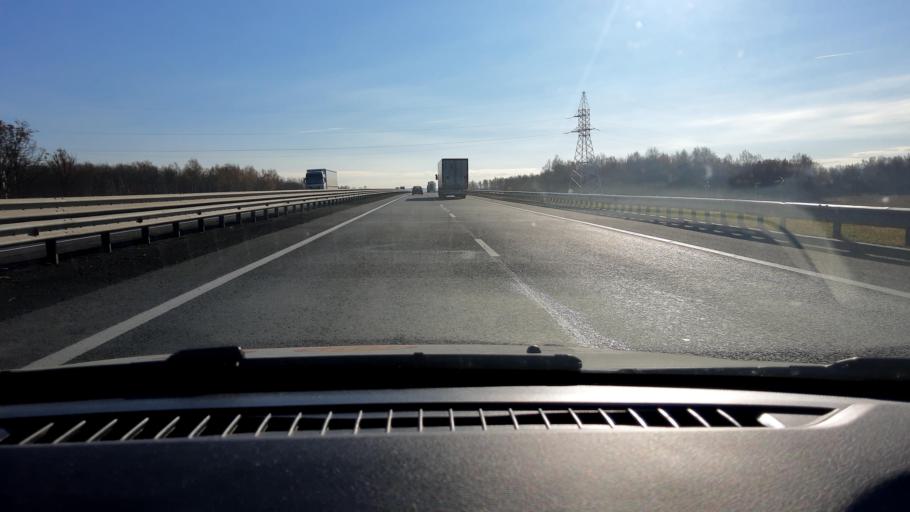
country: RU
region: Nizjnij Novgorod
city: Burevestnik
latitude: 56.1370
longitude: 43.7680
